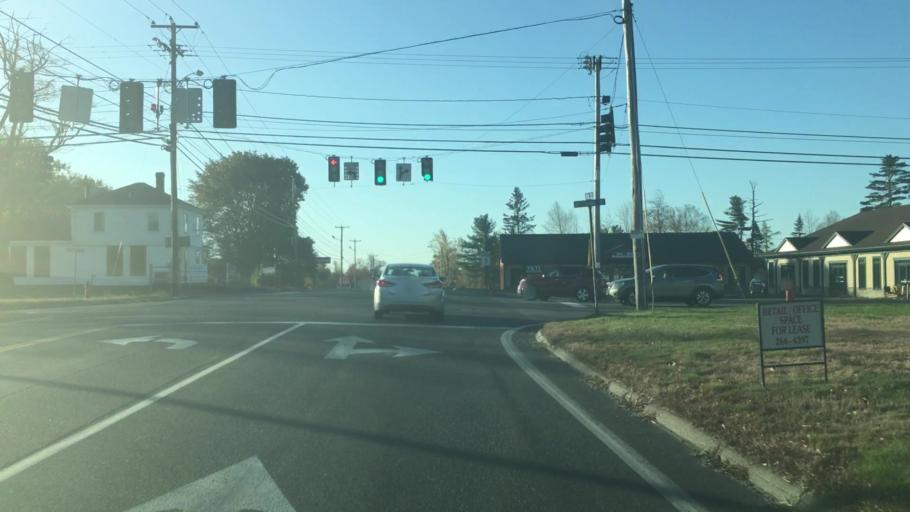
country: US
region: Maine
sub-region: Hancock County
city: Ellsworth
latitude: 44.5196
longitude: -68.3961
